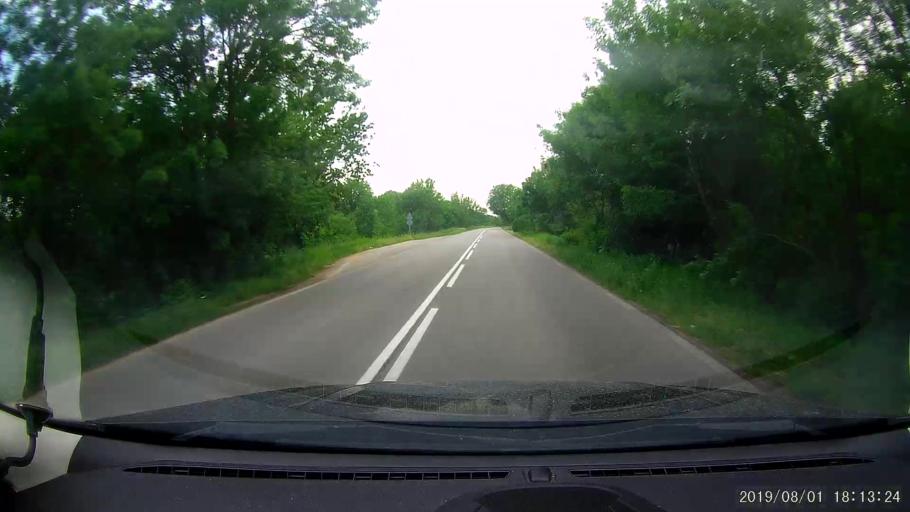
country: BG
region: Silistra
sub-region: Obshtina Dulovo
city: Dulovo
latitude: 43.7900
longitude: 27.1403
